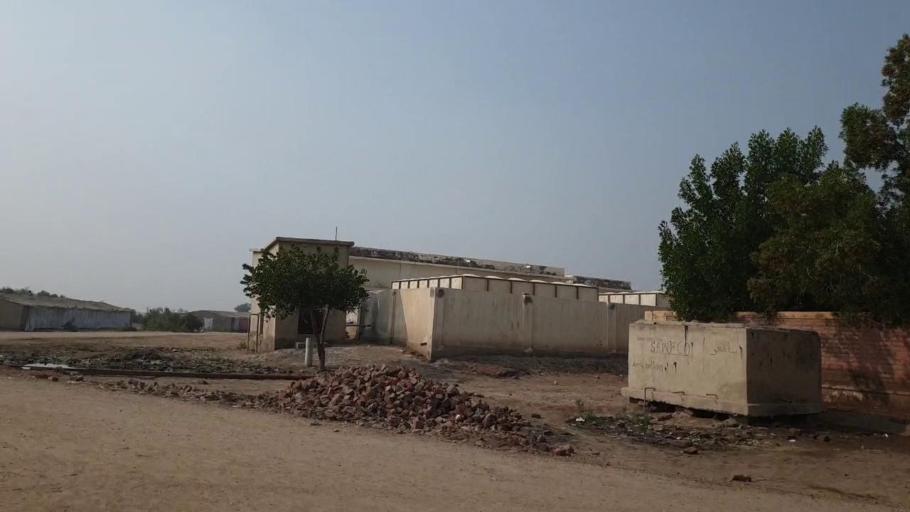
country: PK
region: Sindh
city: Bhan
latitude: 26.5082
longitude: 67.6908
